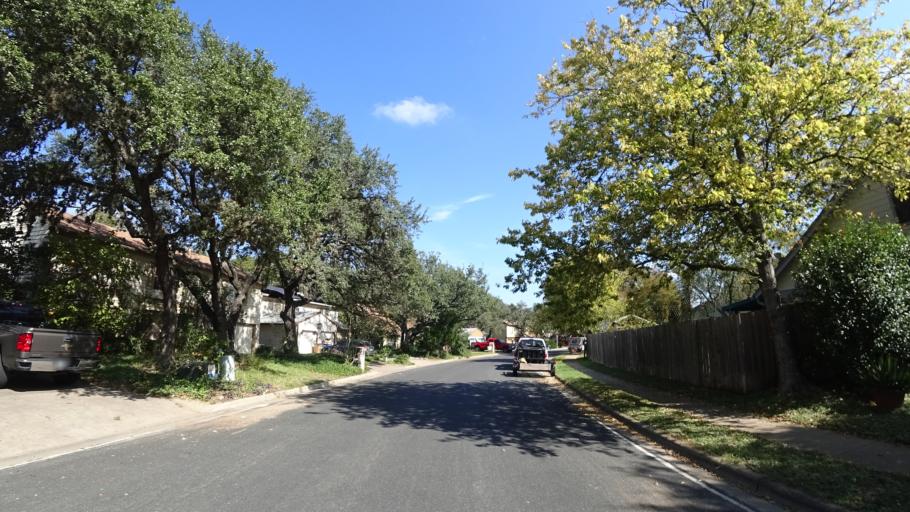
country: US
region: Texas
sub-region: Travis County
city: Shady Hollow
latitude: 30.2139
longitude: -97.8268
